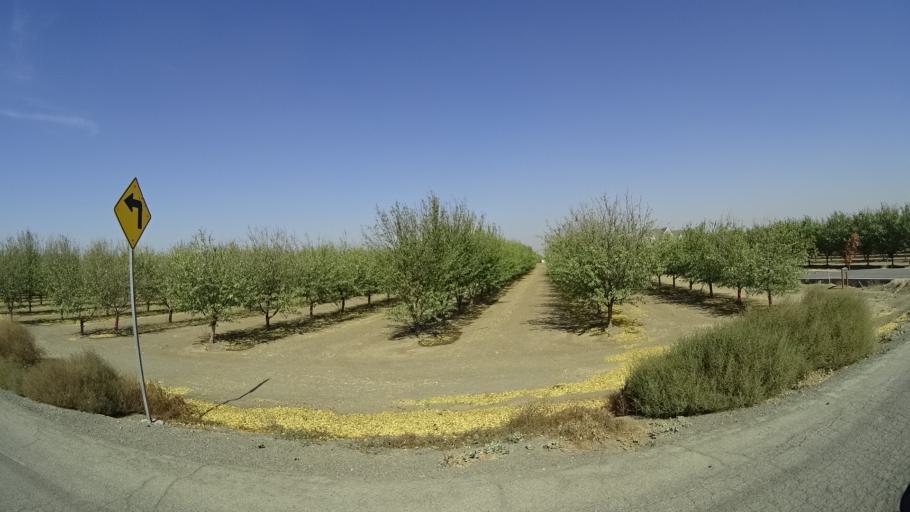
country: US
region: California
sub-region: Yolo County
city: Davis
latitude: 38.5668
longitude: -121.6918
